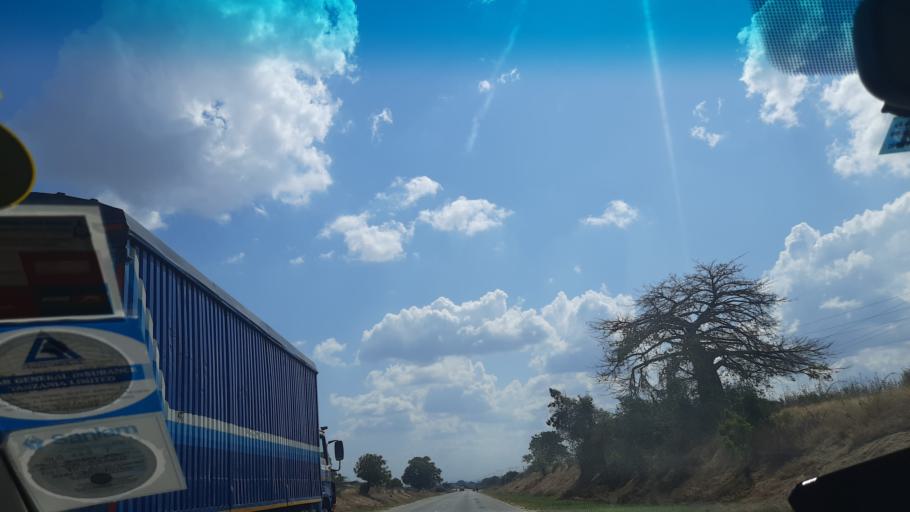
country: TZ
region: Singida
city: Kintinku
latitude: -5.9477
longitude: 35.3101
